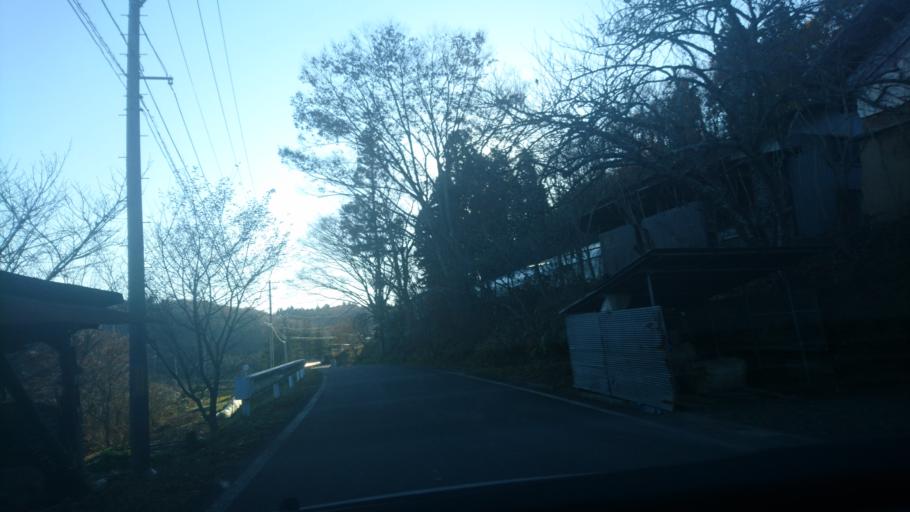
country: JP
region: Iwate
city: Ichinoseki
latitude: 38.8991
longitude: 141.2053
